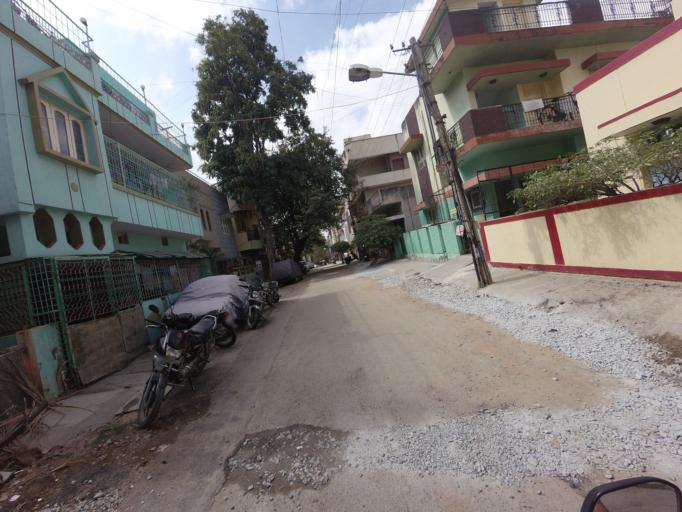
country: IN
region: Karnataka
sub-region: Bangalore Urban
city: Bangalore
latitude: 12.9617
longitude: 77.5367
